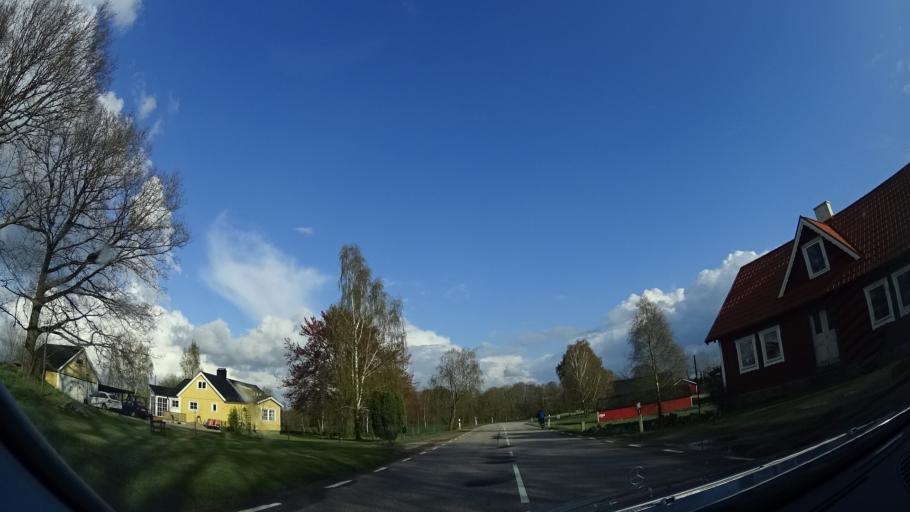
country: SE
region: Skane
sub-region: Klippans Kommun
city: Ljungbyhed
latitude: 56.0233
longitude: 13.2713
